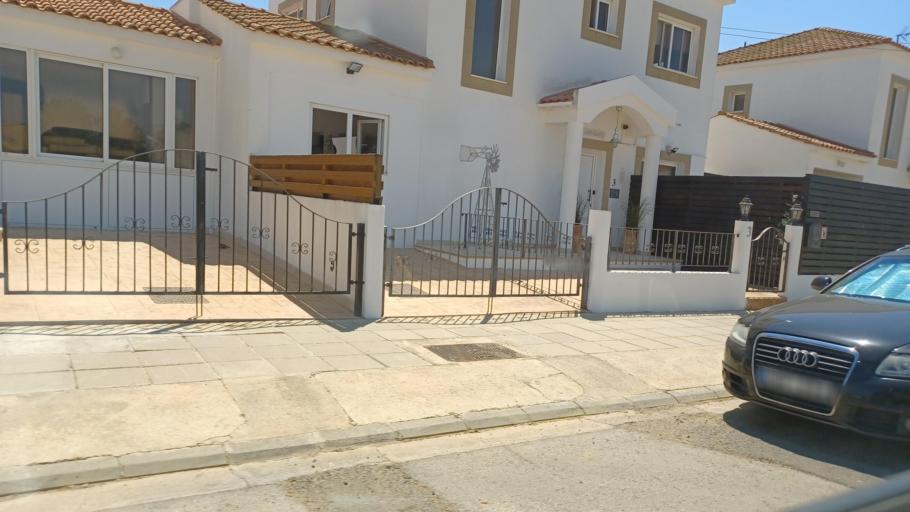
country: CY
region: Ammochostos
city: Acheritou
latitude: 35.0719
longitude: 33.8864
